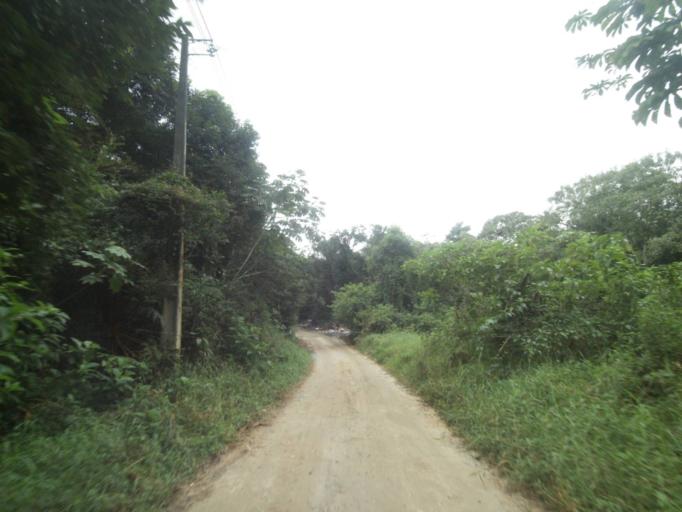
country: BR
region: Parana
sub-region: Paranagua
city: Paranagua
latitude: -25.5402
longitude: -48.5530
